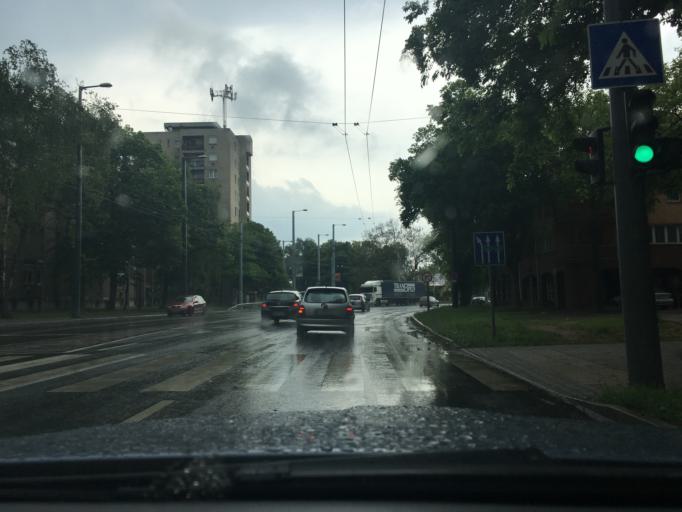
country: HU
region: Hajdu-Bihar
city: Debrecen
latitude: 47.5217
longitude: 21.6227
